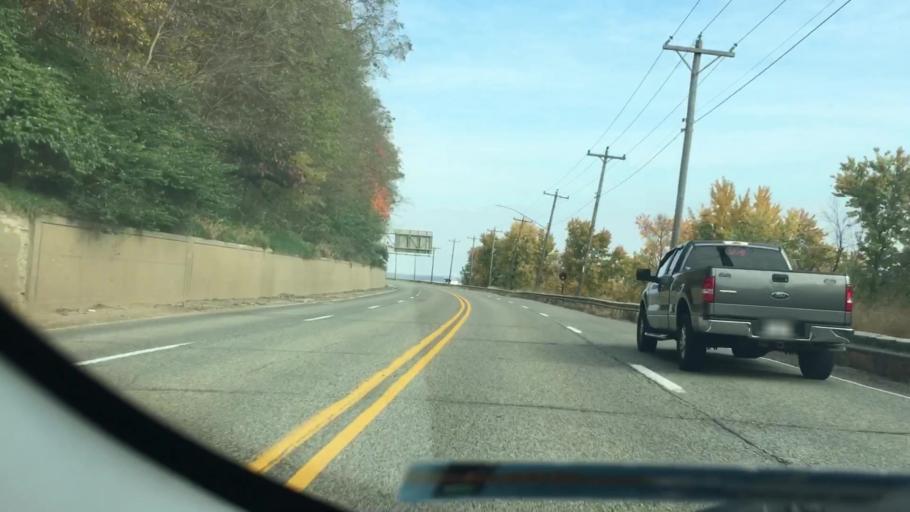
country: US
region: Illinois
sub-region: Peoria County
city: Peoria Heights
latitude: 40.7280
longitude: -89.5518
